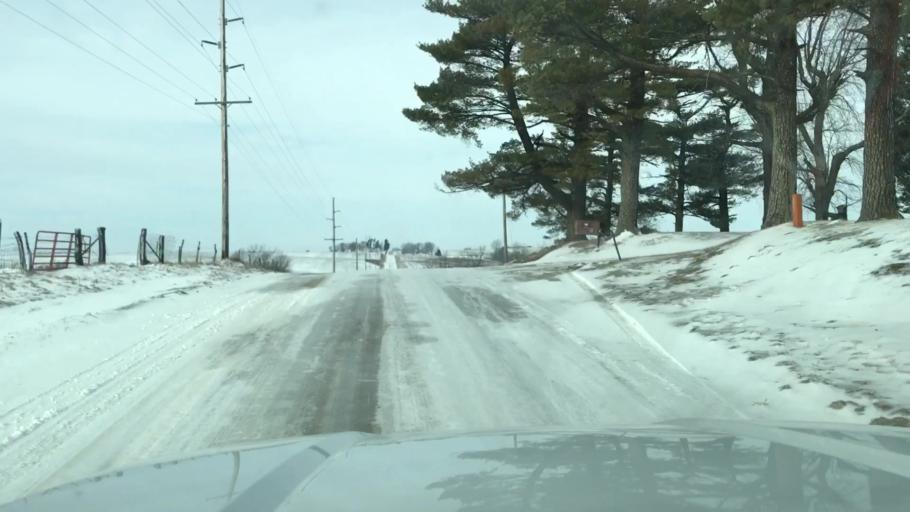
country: US
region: Missouri
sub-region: Holt County
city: Mound City
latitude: 40.1301
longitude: -95.0751
